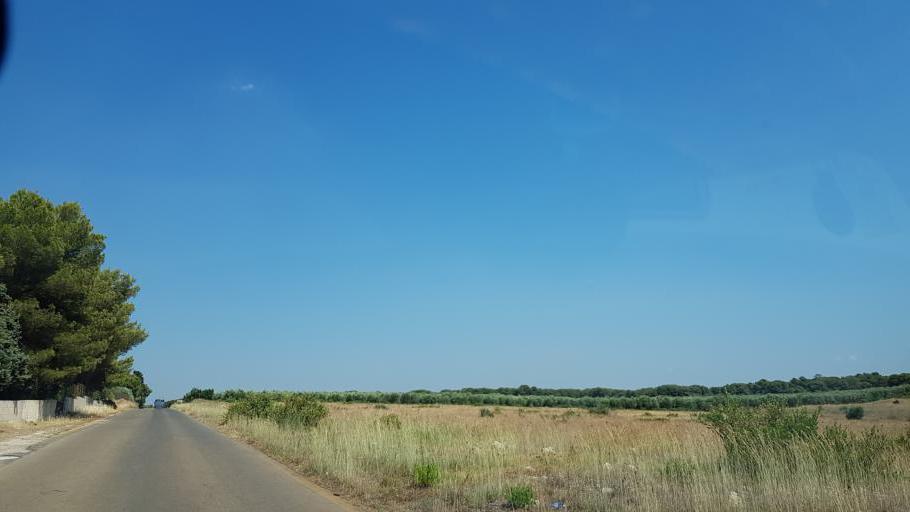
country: IT
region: Apulia
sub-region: Provincia di Lecce
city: Nardo
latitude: 40.1743
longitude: 17.9489
